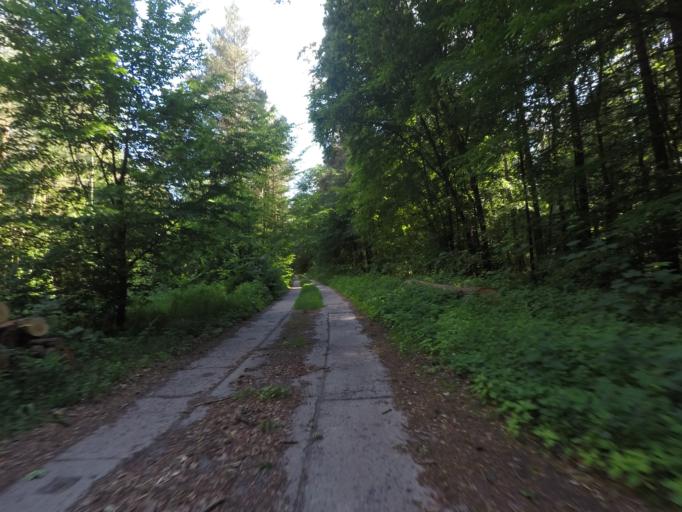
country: DE
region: Brandenburg
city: Britz
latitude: 52.8639
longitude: 13.7847
